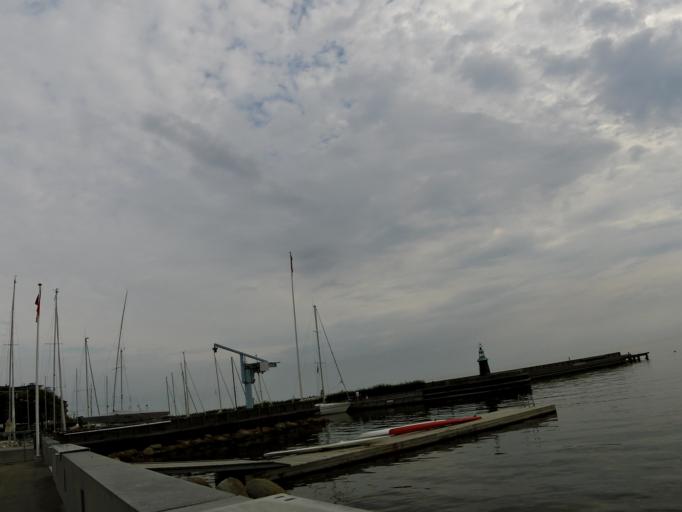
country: DK
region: Capital Region
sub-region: Gentofte Kommune
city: Charlottenlund
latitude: 55.7312
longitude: 12.5815
